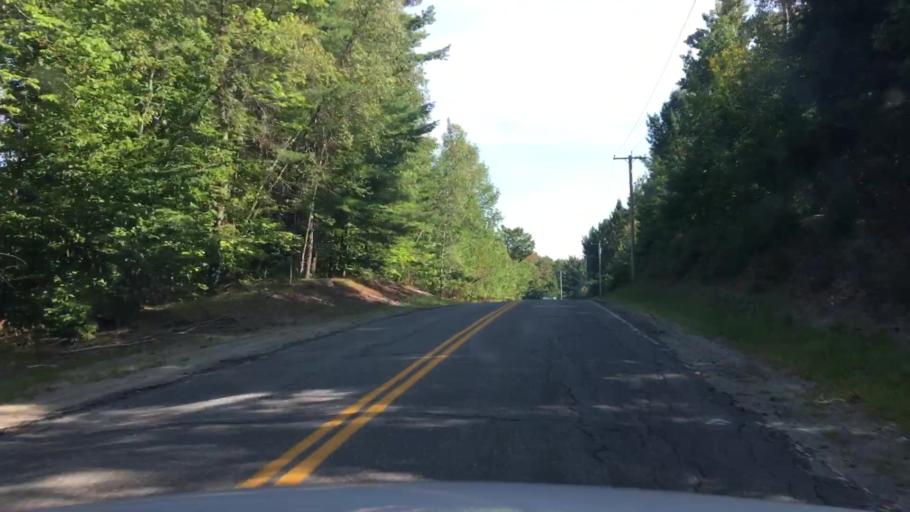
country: US
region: Maine
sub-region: Penobscot County
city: Enfield
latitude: 45.2110
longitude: -68.5238
